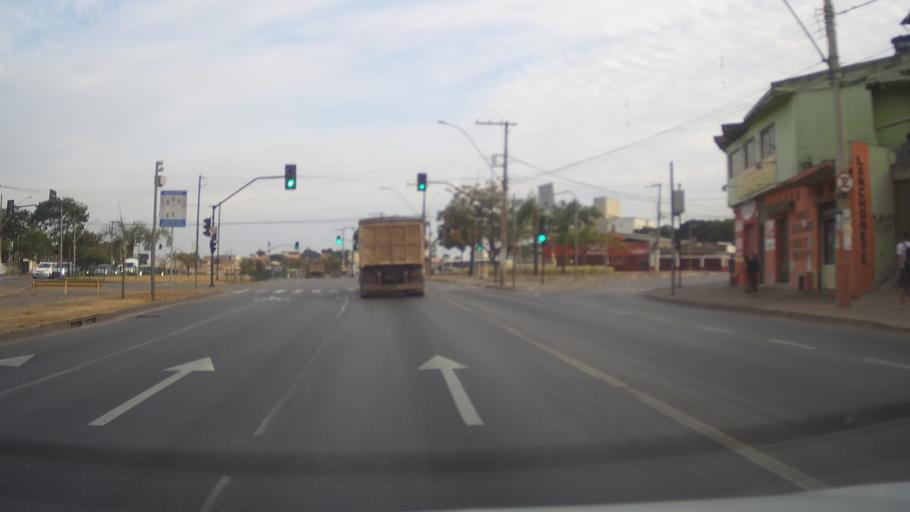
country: BR
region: Minas Gerais
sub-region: Belo Horizonte
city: Belo Horizonte
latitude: -19.8474
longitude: -43.9325
